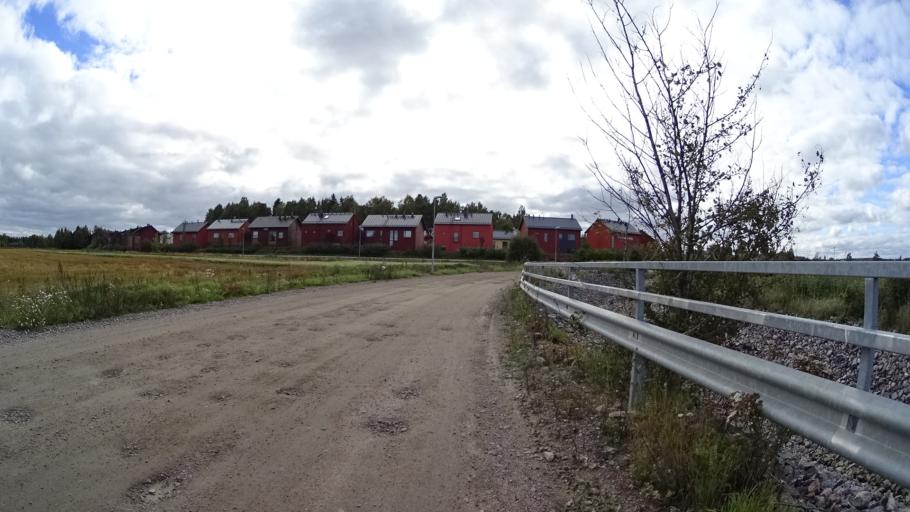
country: FI
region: Uusimaa
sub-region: Helsinki
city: Vantaa
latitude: 60.2660
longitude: 24.9574
